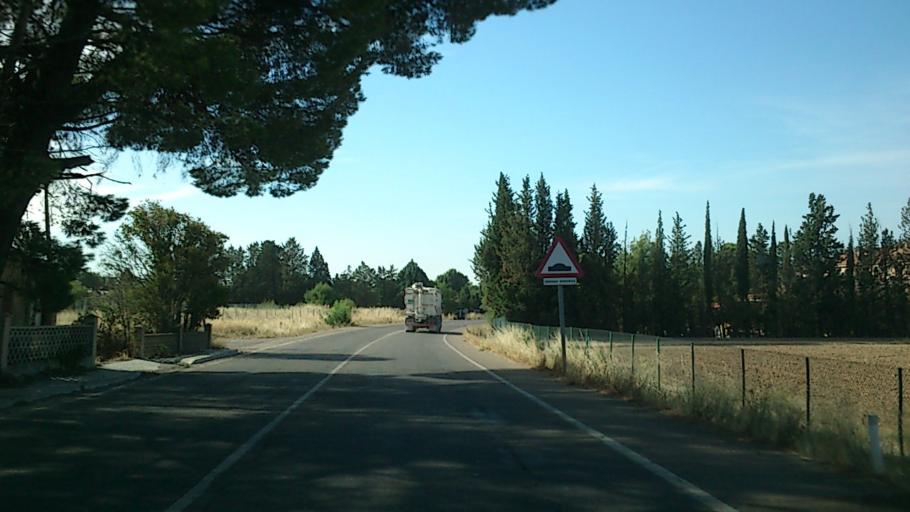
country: ES
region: Aragon
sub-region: Provincia de Zaragoza
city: Villanueva de Gallego
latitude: 41.7270
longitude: -0.8101
